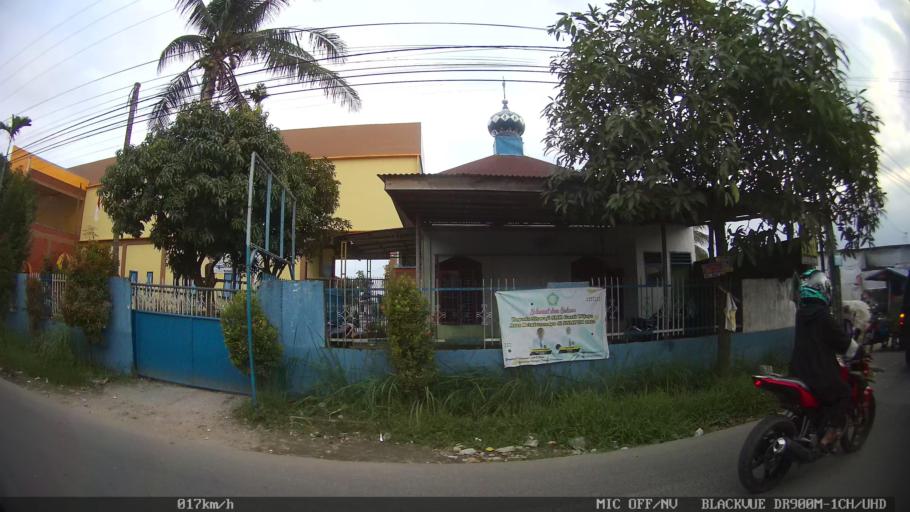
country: ID
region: North Sumatra
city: Sunggal
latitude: 3.5639
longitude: 98.5986
